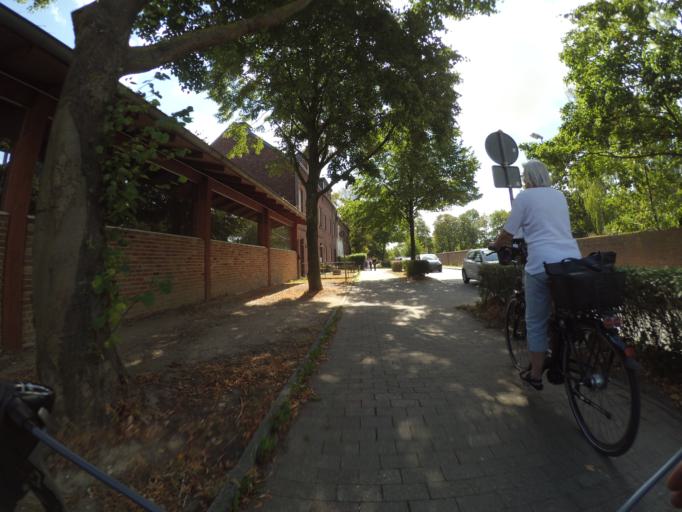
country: DE
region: North Rhine-Westphalia
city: Julich
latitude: 50.9010
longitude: 6.3509
